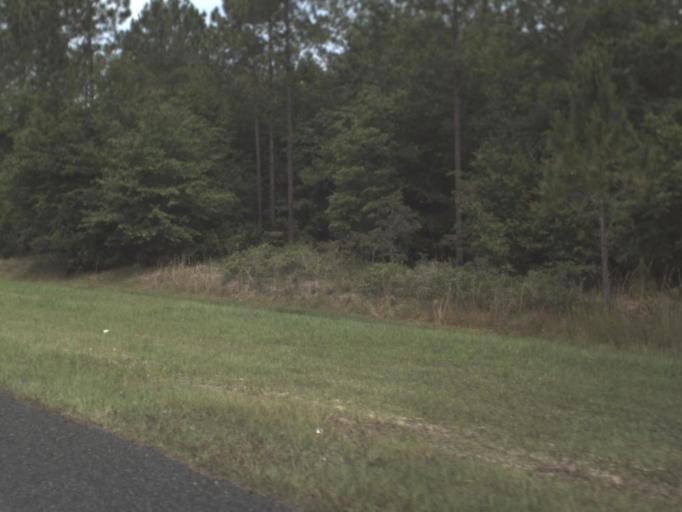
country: US
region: Florida
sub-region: Alachua County
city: Hawthorne
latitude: 29.5995
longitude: -82.1683
